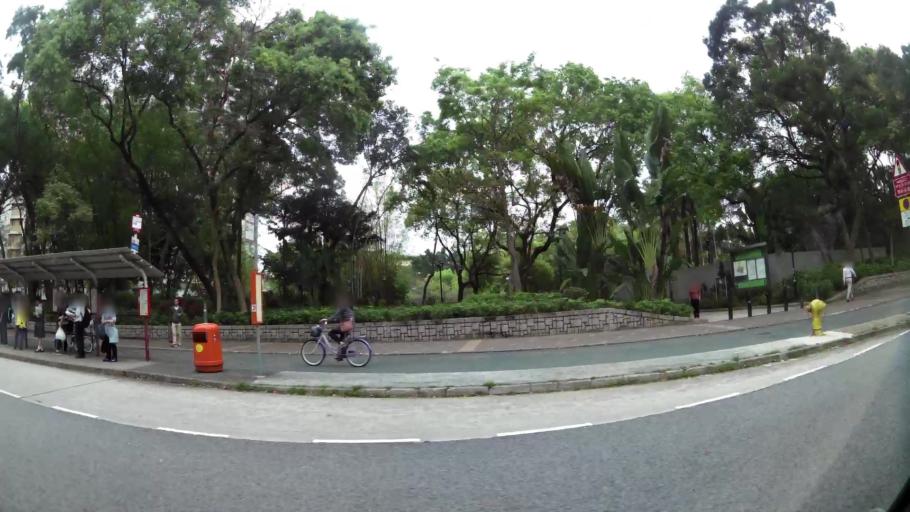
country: HK
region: Tai Po
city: Tai Po
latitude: 22.4521
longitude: 114.1655
